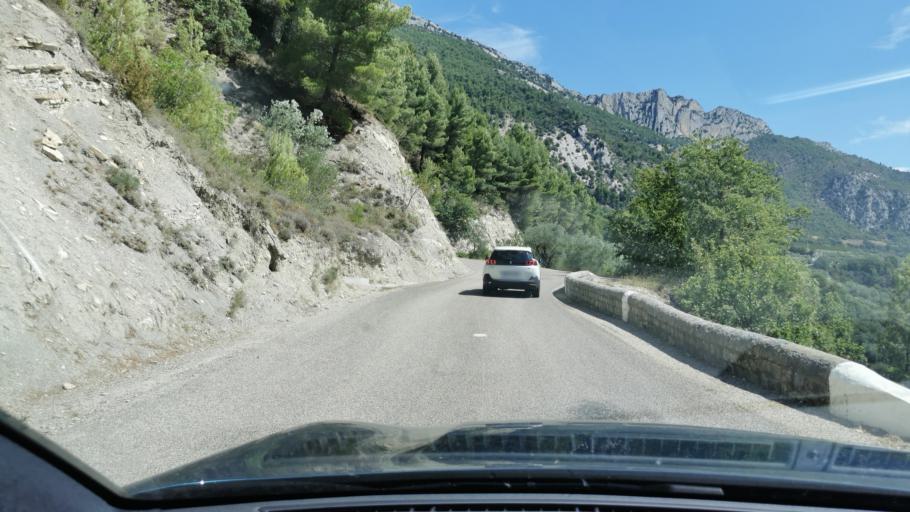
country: FR
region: Rhone-Alpes
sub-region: Departement de la Drome
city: Buis-les-Baronnies
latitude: 44.2991
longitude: 5.2857
